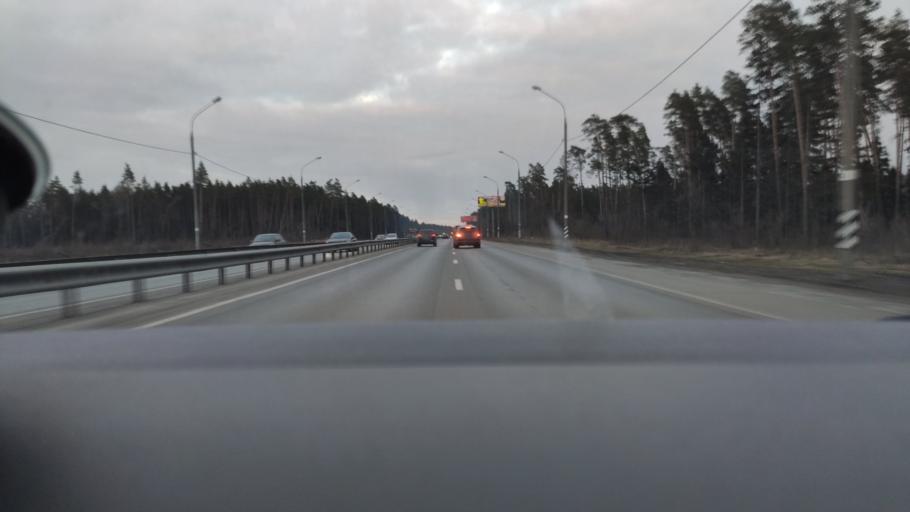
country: RU
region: Moskovskaya
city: Monino
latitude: 55.8241
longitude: 38.1992
